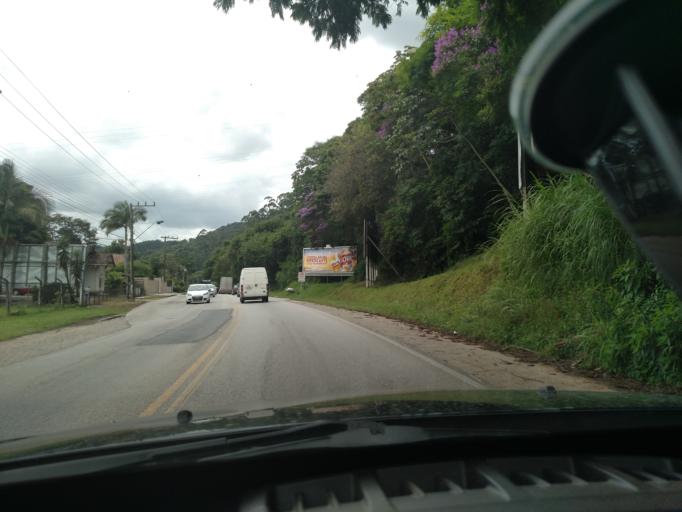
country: BR
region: Santa Catarina
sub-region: Blumenau
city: Blumenau
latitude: -26.9091
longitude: -49.0299
